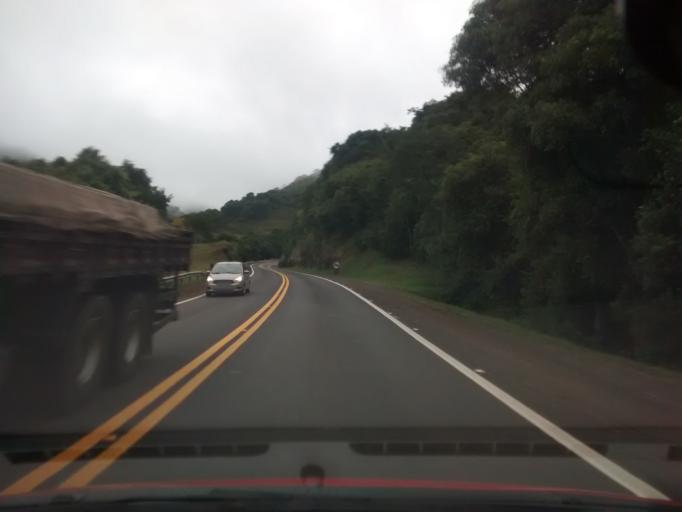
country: BR
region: Rio Grande do Sul
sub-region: Vacaria
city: Estrela
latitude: -28.1966
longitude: -50.7437
